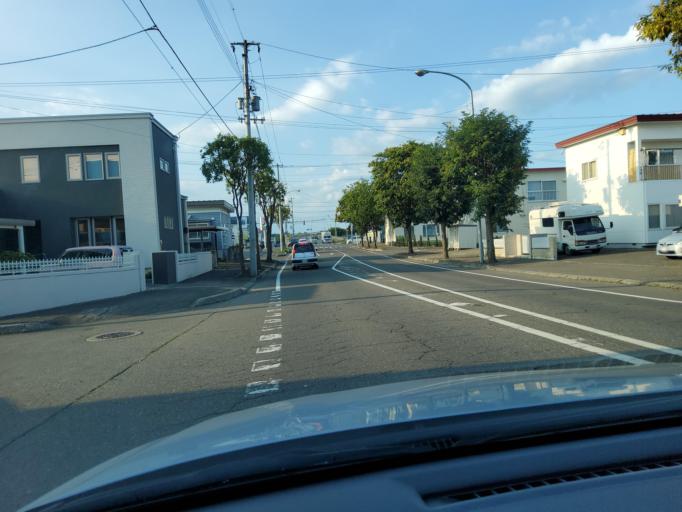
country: JP
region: Hokkaido
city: Obihiro
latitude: 42.9396
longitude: 143.1838
